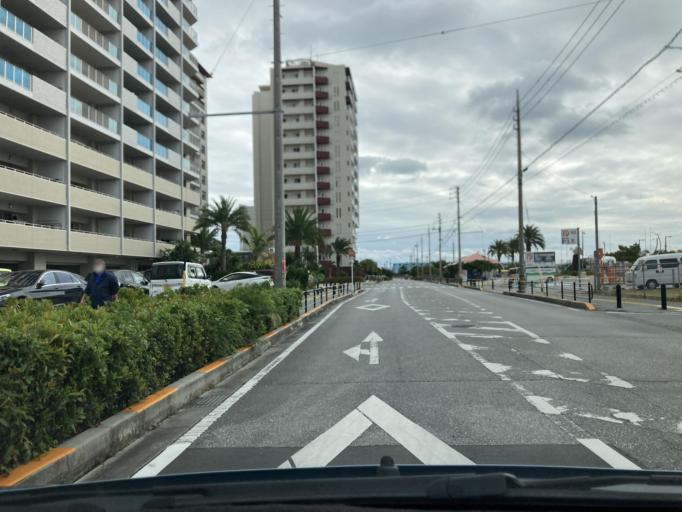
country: JP
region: Okinawa
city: Itoman
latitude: 26.1550
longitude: 127.6590
